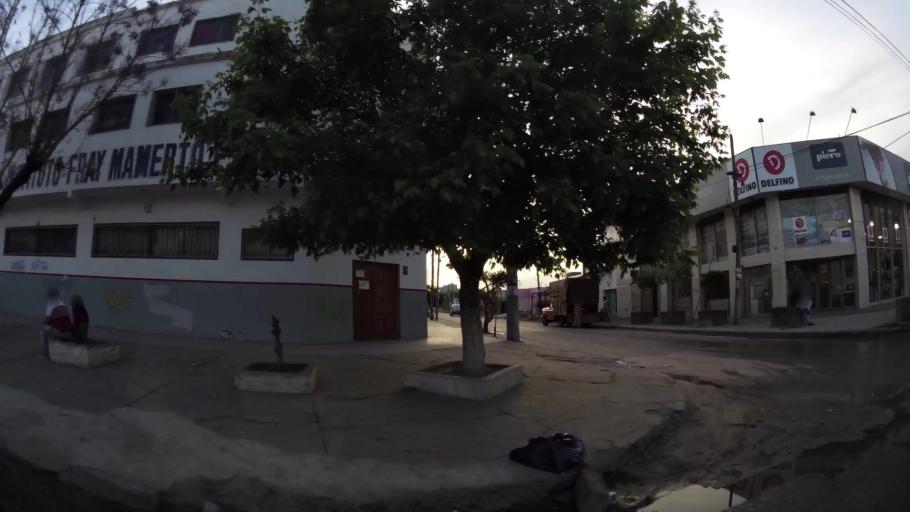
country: AR
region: Buenos Aires
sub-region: Partido de Almirante Brown
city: Adrogue
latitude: -34.7841
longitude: -58.3166
